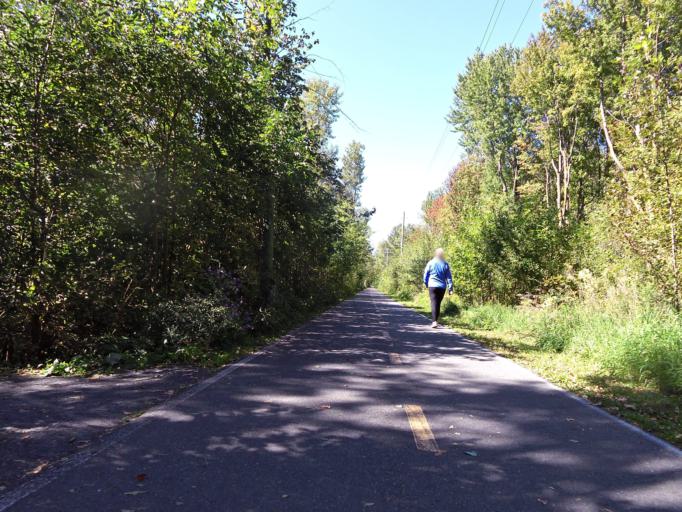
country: CA
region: Ontario
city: Bourget
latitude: 45.2715
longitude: -75.3022
